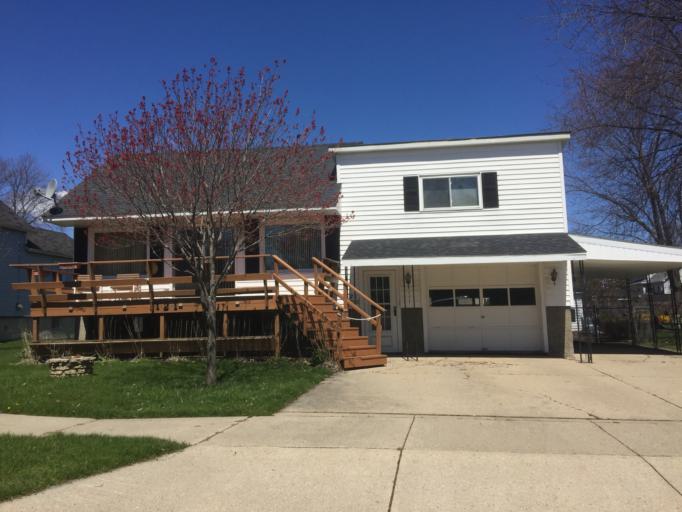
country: US
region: Michigan
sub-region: Menominee County
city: Menominee
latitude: 45.0867
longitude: -87.5964
